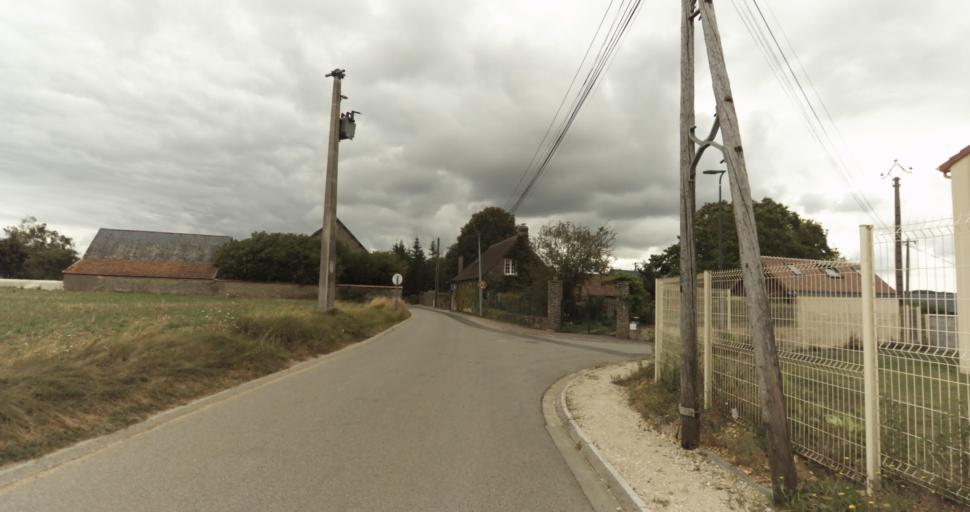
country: FR
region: Haute-Normandie
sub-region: Departement de l'Eure
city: Menilles
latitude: 49.0239
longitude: 1.3060
